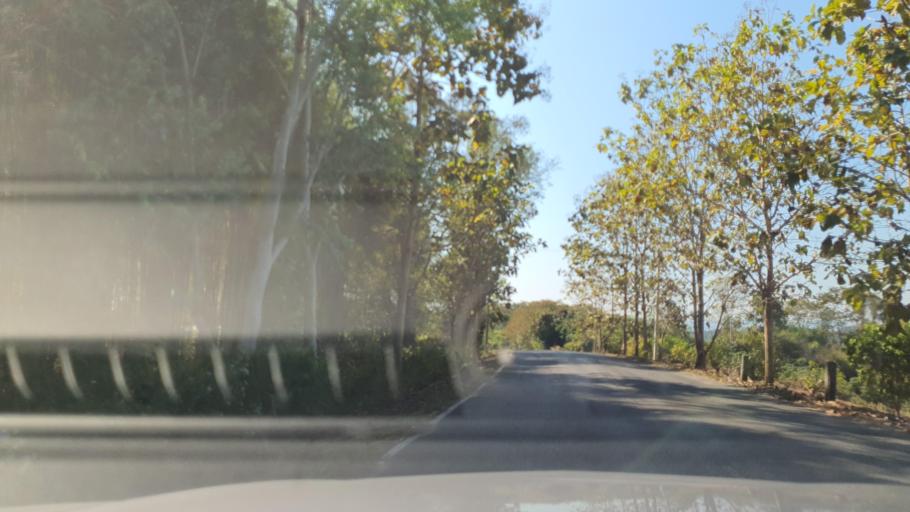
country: TH
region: Nan
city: Pua
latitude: 19.1188
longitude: 100.9138
